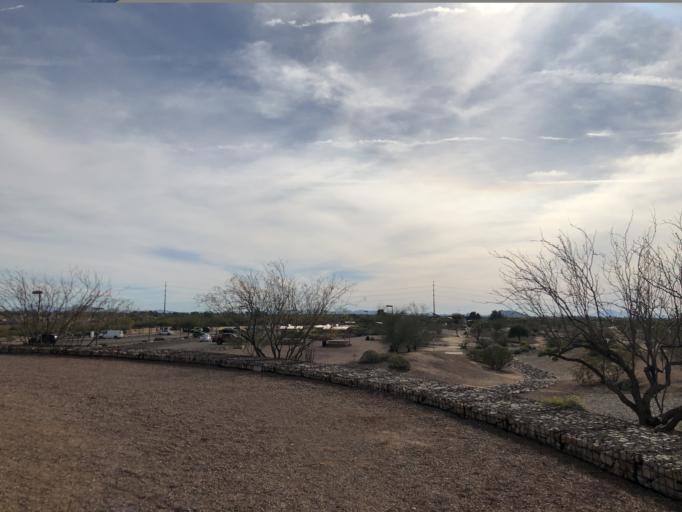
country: US
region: Arizona
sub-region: Maricopa County
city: Chandler
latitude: 33.2520
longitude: -111.8260
